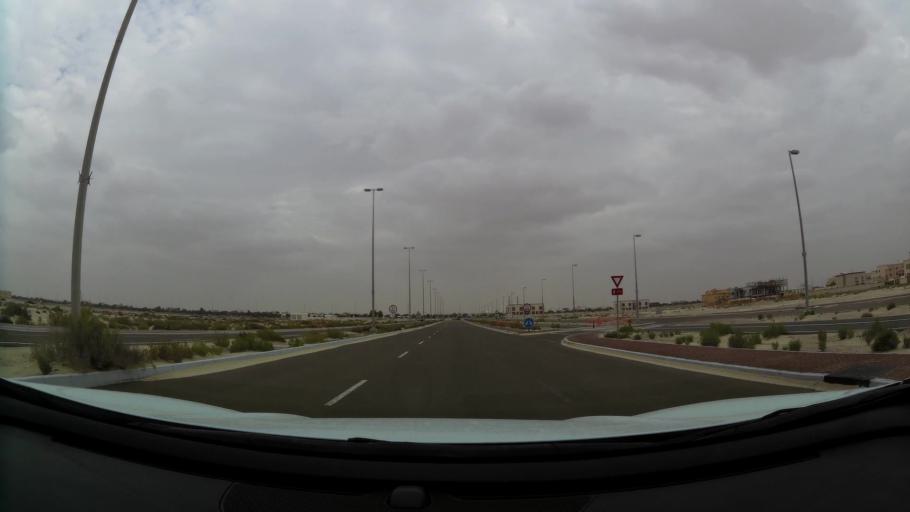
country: AE
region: Abu Dhabi
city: Abu Dhabi
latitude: 24.3578
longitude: 54.6392
